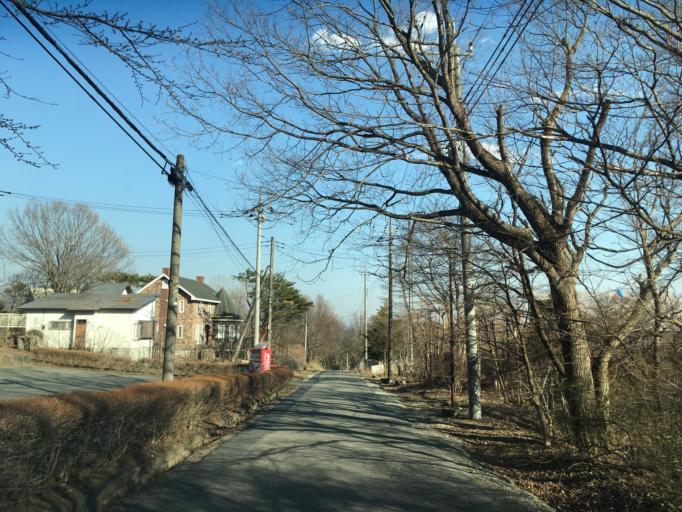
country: JP
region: Tochigi
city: Kuroiso
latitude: 37.0689
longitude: 140.0007
